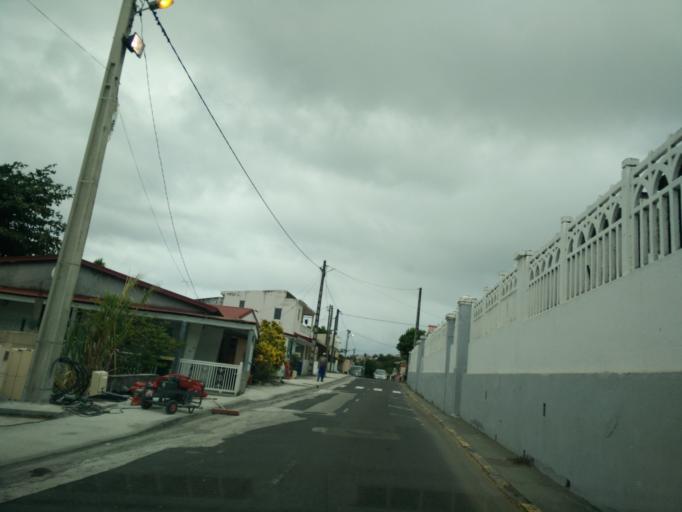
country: MQ
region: Martinique
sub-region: Martinique
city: Saint-Pierre
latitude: 14.7947
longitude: -61.2205
